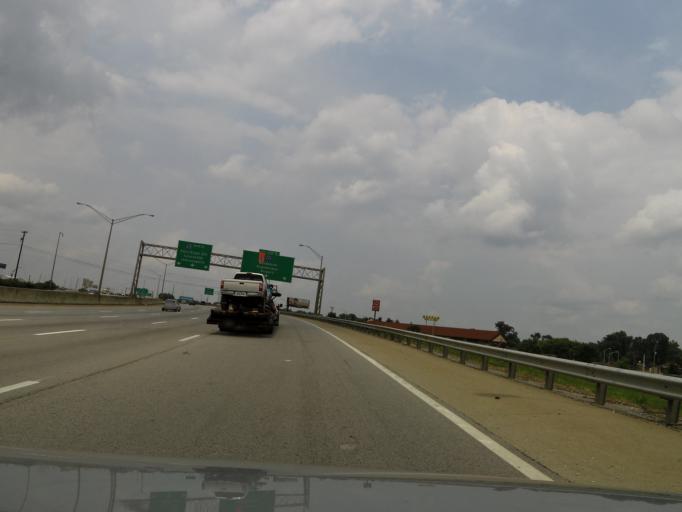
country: US
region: Kentucky
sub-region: Jefferson County
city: Audubon Park
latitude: 38.1770
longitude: -85.7191
